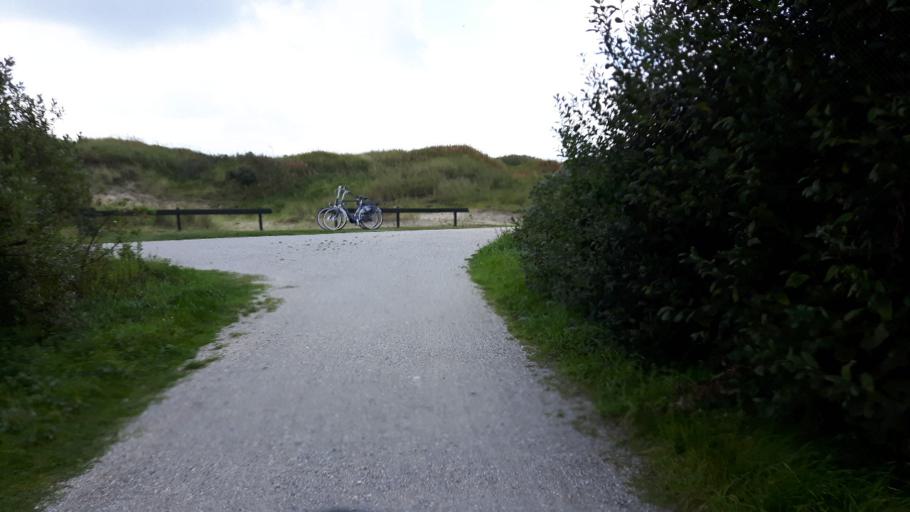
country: NL
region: Friesland
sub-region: Gemeente Dongeradeel
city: Holwerd
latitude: 53.4618
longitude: 5.8992
